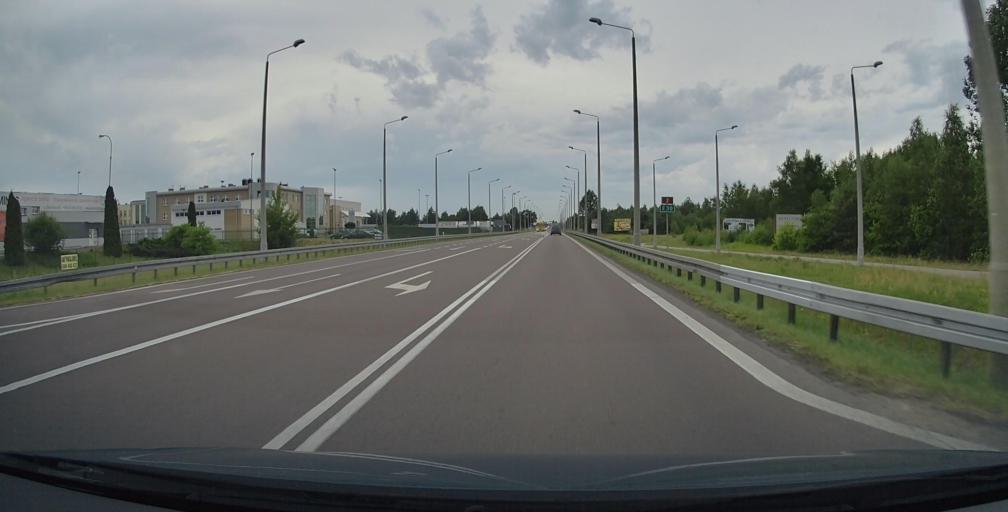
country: PL
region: Lublin Voivodeship
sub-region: Biala Podlaska
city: Biala Podlaska
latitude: 52.0463
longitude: 23.1509
